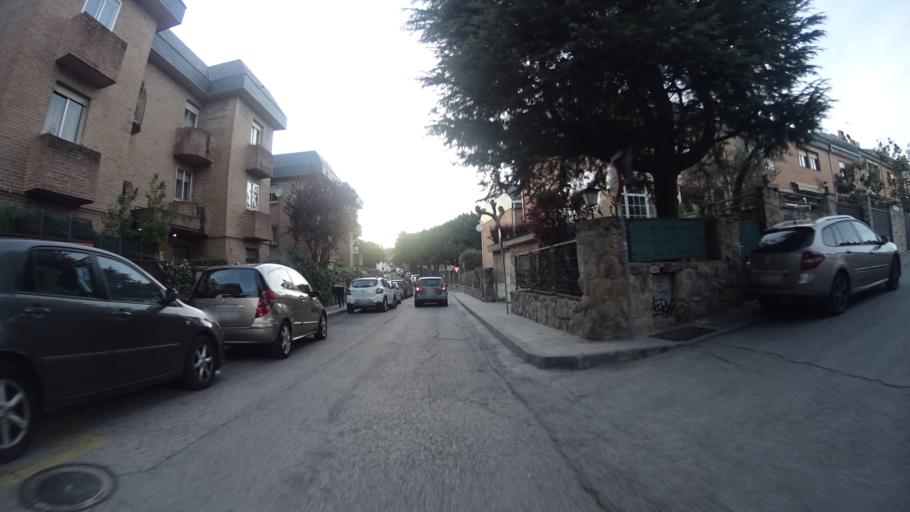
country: ES
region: Madrid
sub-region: Provincia de Madrid
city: Torrelodones
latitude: 40.5771
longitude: -3.9269
